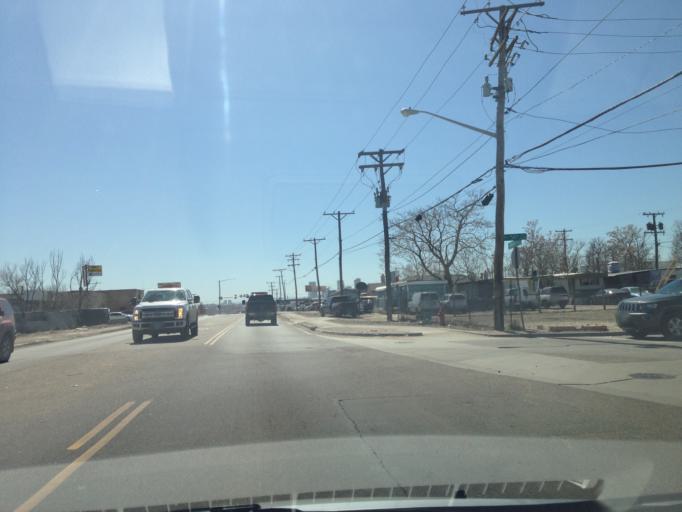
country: US
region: Colorado
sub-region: Adams County
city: Twin Lakes
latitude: 39.7986
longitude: -104.9782
